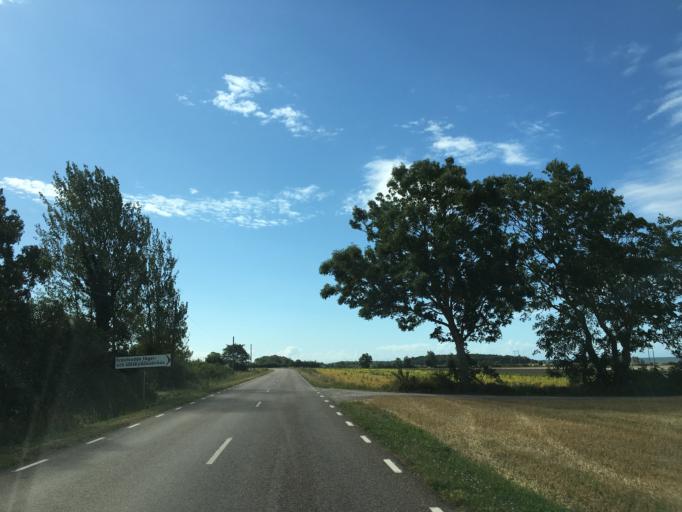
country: SE
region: Kalmar
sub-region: Morbylanga Kommun
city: Moerbylanga
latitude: 56.4154
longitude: 16.4136
